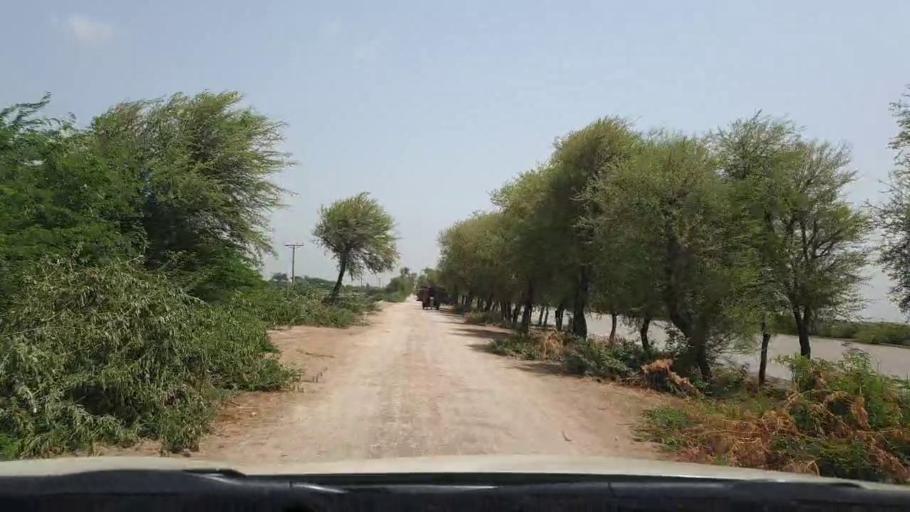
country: PK
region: Sindh
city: Talhar
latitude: 24.9146
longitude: 68.8386
